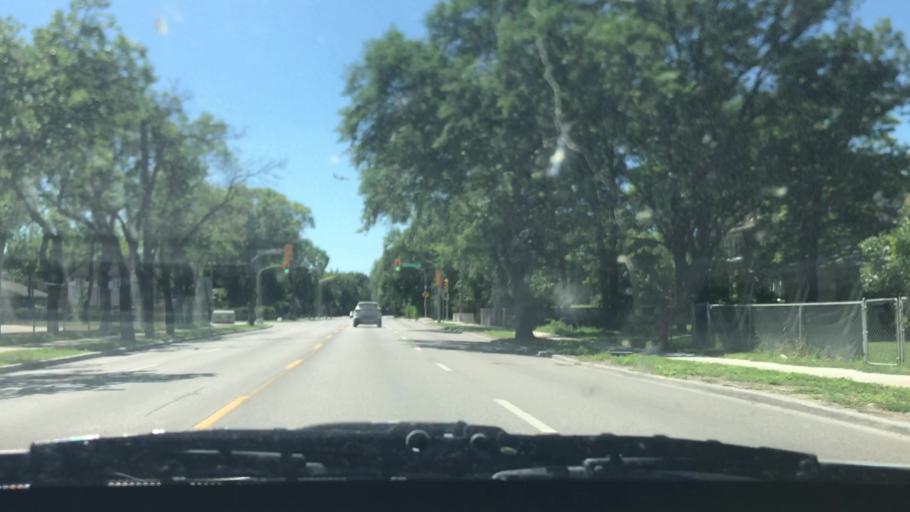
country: CA
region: Manitoba
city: Winnipeg
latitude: 49.8747
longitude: -97.1681
